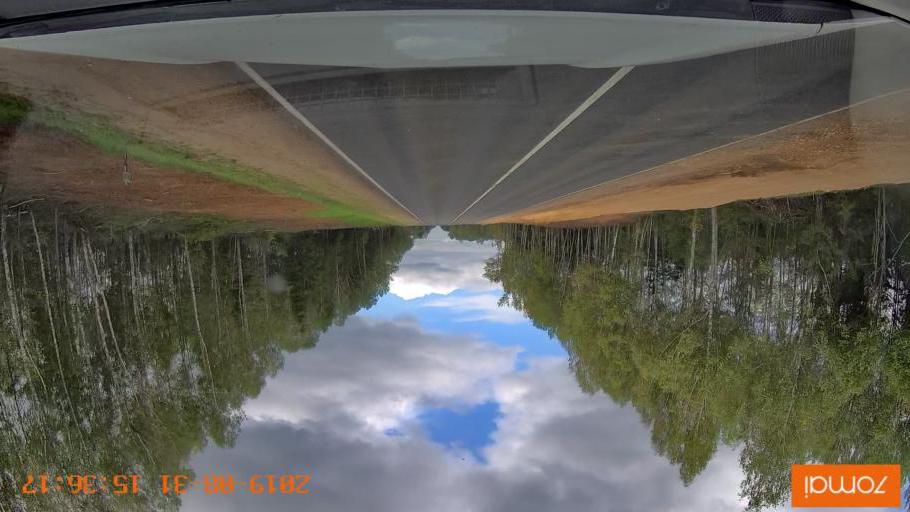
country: RU
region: Kaluga
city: Mosal'sk
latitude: 54.6102
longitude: 34.7551
